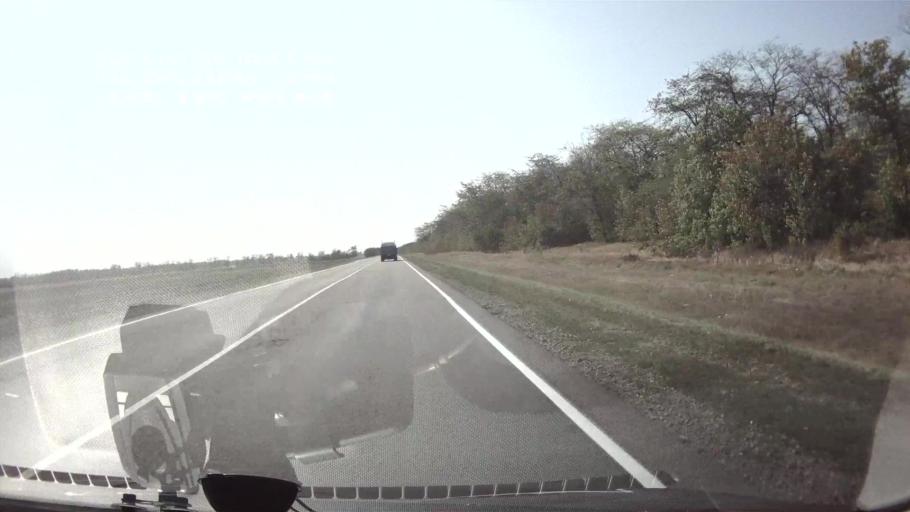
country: RU
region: Krasnodarskiy
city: Novopokrovskaya
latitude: 45.8250
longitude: 40.7201
